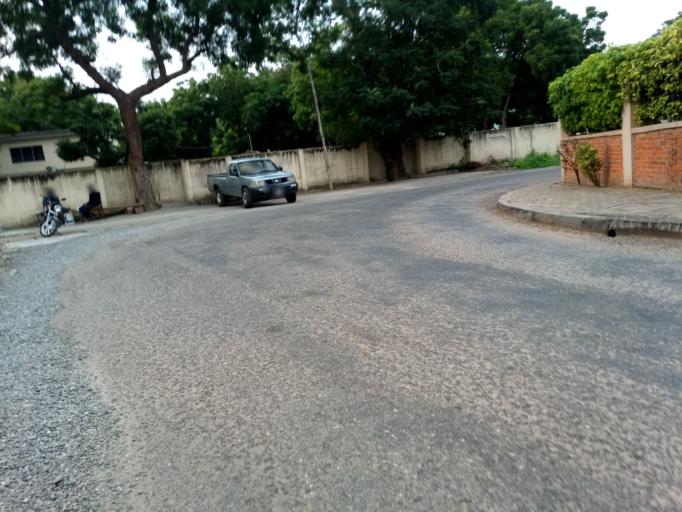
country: GH
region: Greater Accra
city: Accra
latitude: 5.5617
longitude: -0.1906
